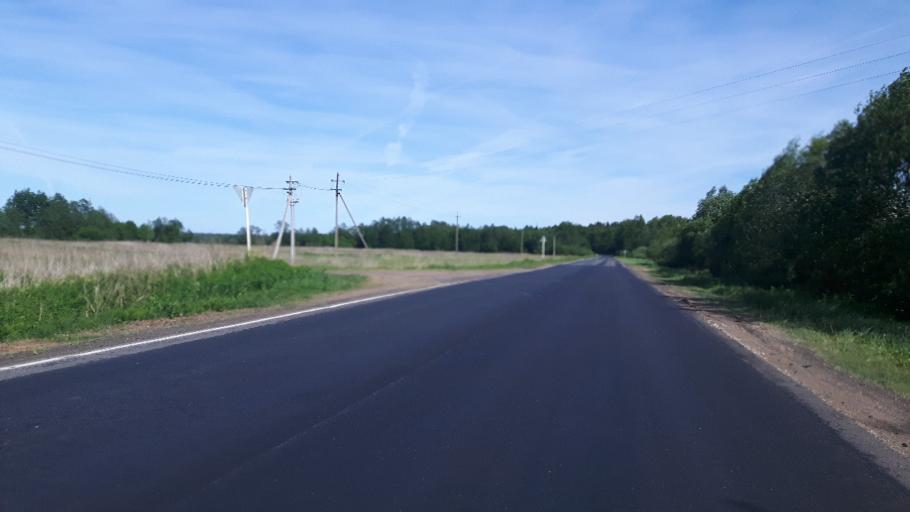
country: RU
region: Leningrad
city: Ivangorod
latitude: 59.4185
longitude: 28.3607
